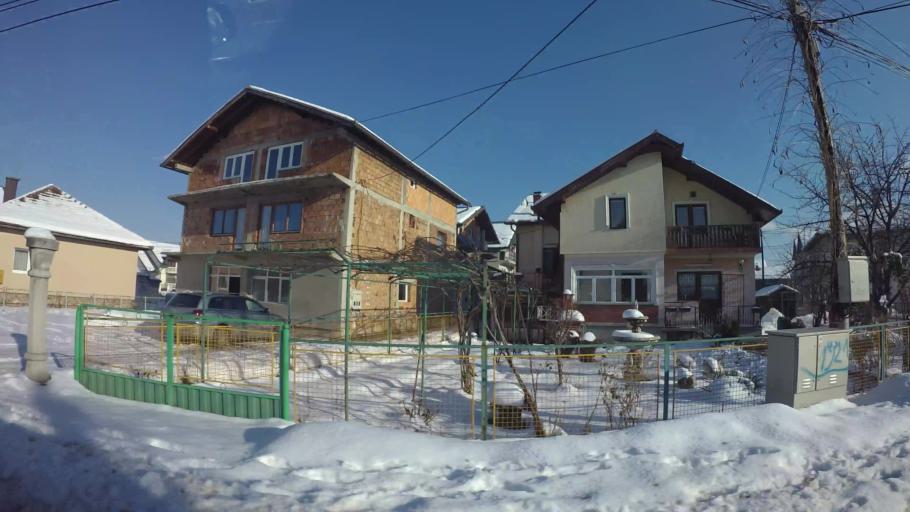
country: BA
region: Federation of Bosnia and Herzegovina
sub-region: Kanton Sarajevo
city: Sarajevo
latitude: 43.8200
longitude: 18.3308
